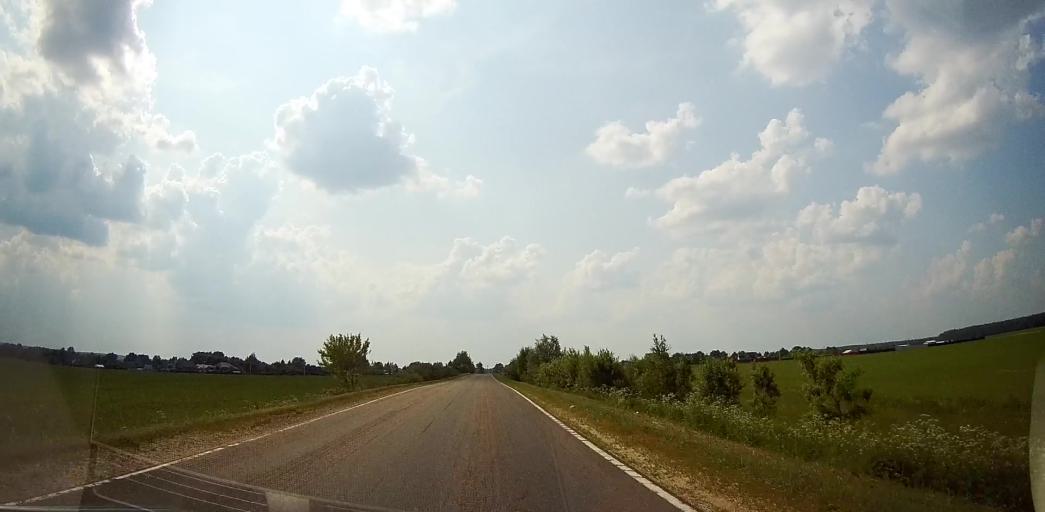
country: RU
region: Moskovskaya
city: Malino
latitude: 55.0643
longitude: 38.1125
